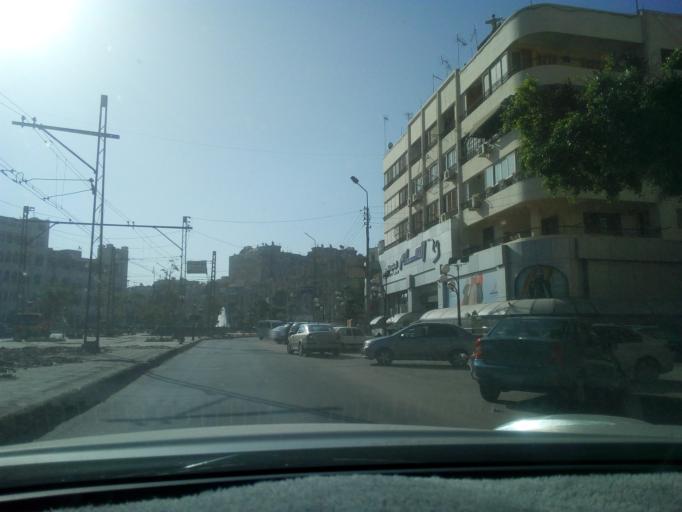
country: EG
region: Muhafazat al Qahirah
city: Cairo
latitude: 30.0974
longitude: 31.3341
